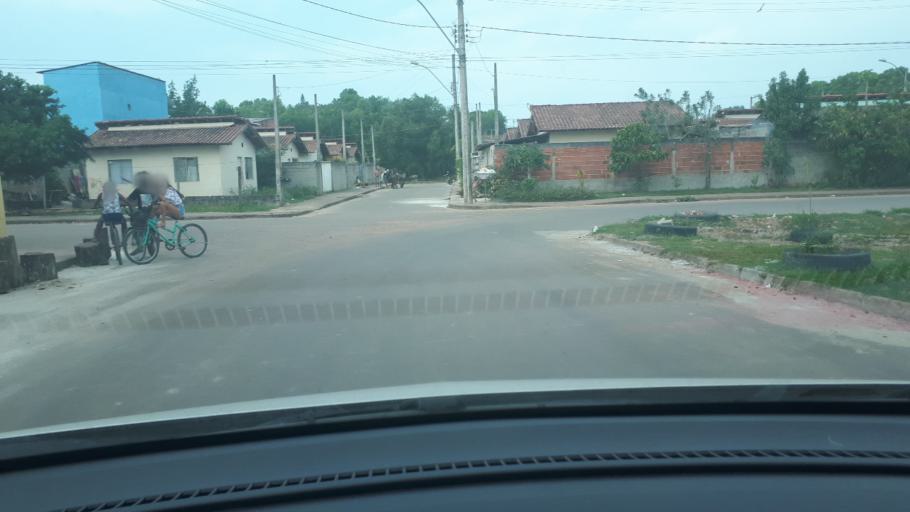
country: BR
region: Espirito Santo
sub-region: Serra
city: Serra
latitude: -20.1447
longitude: -40.1923
